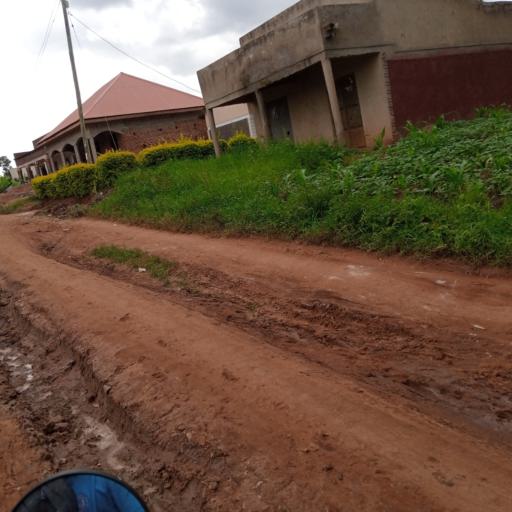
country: UG
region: Eastern Region
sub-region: Mbale District
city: Mbale
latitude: 1.1245
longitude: 34.1739
